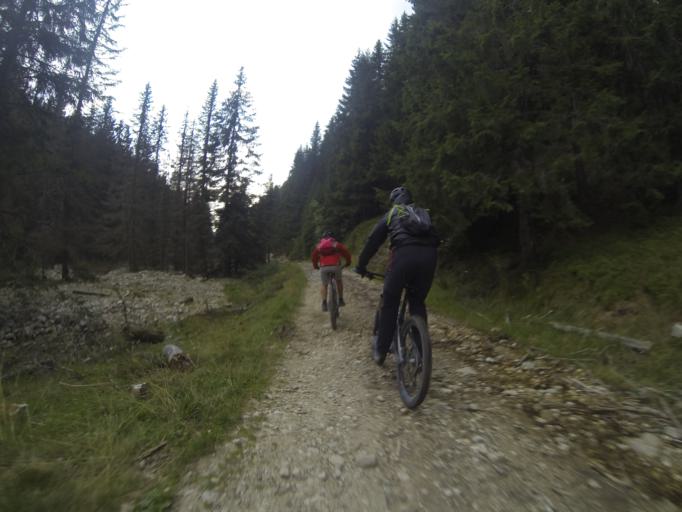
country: RO
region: Gorj
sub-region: Comuna Polovragi
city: Polovragi
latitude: 45.2930
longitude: 23.8462
